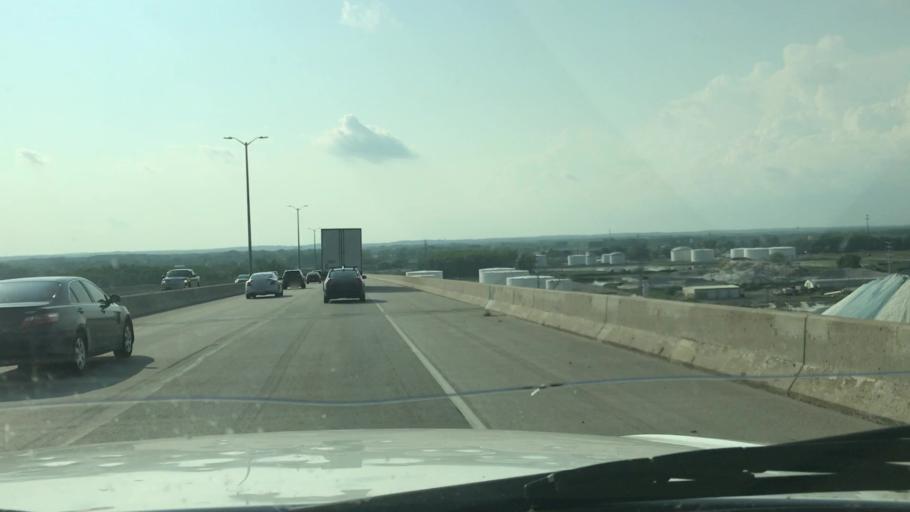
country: US
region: Wisconsin
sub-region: Brown County
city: Green Bay
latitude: 44.5344
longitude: -88.0114
